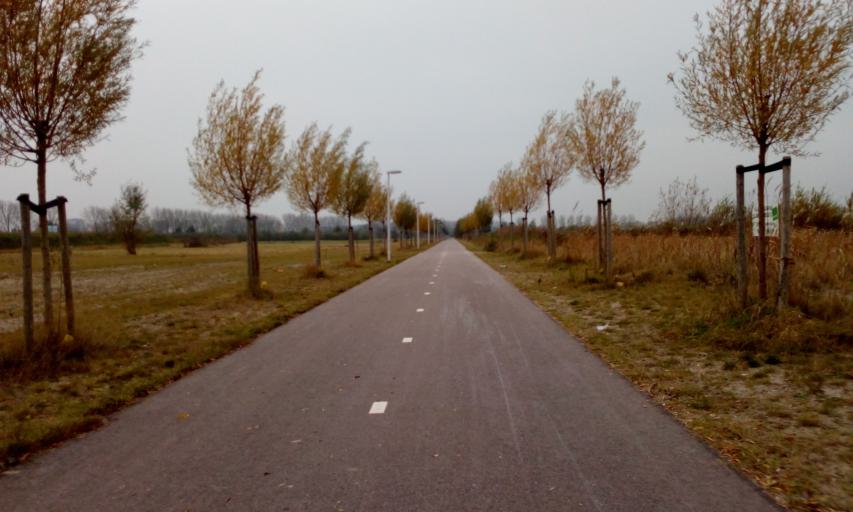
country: NL
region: South Holland
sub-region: Gemeente Lansingerland
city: Bergschenhoek
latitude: 51.9805
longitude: 4.4885
